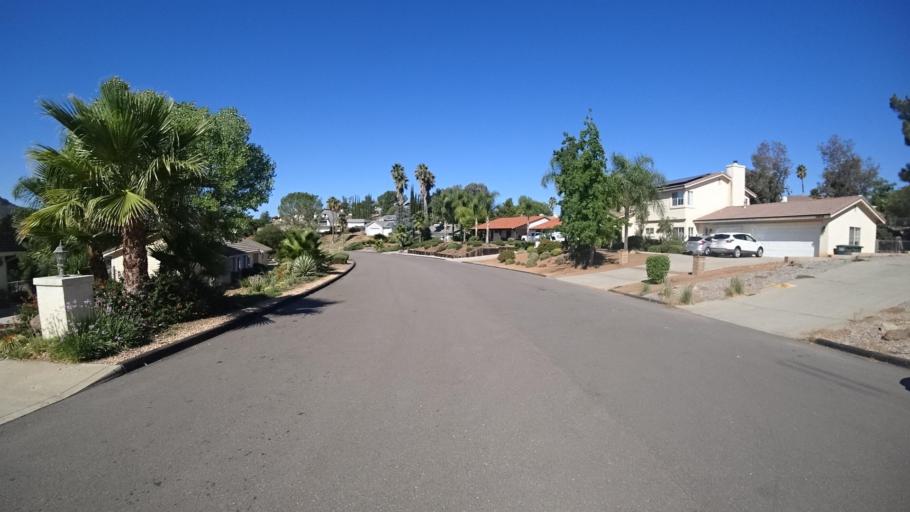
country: US
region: California
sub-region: San Diego County
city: San Diego Country Estates
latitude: 33.0053
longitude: -116.7914
